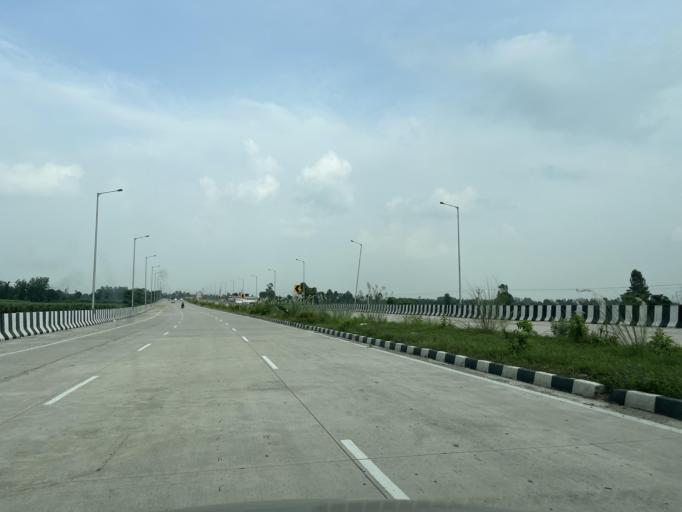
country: IN
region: Uttarakhand
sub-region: Udham Singh Nagar
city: Bazpur
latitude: 29.1494
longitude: 79.0611
